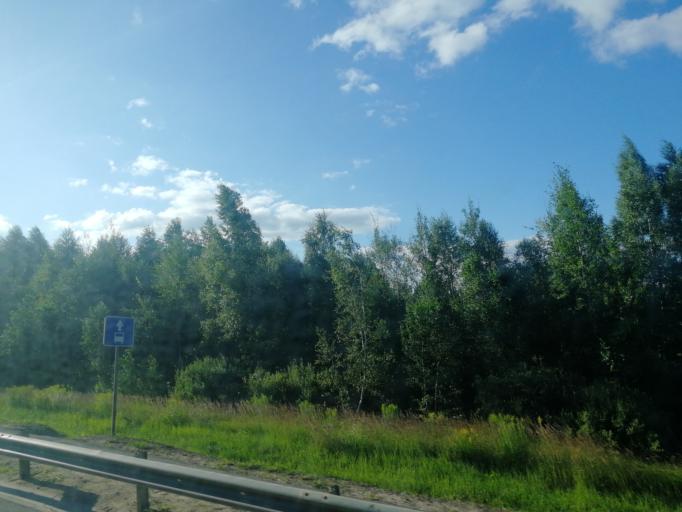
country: RU
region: Tula
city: Novogurovskiy
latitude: 54.2808
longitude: 37.1870
